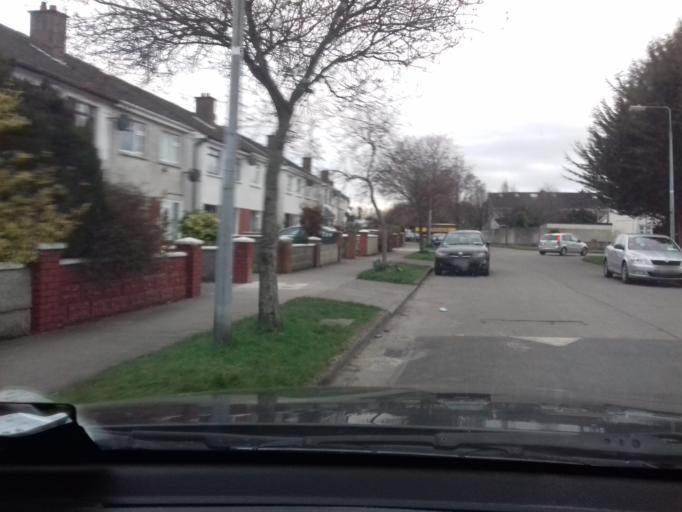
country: IE
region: Leinster
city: Hartstown
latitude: 53.3966
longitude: -6.4198
